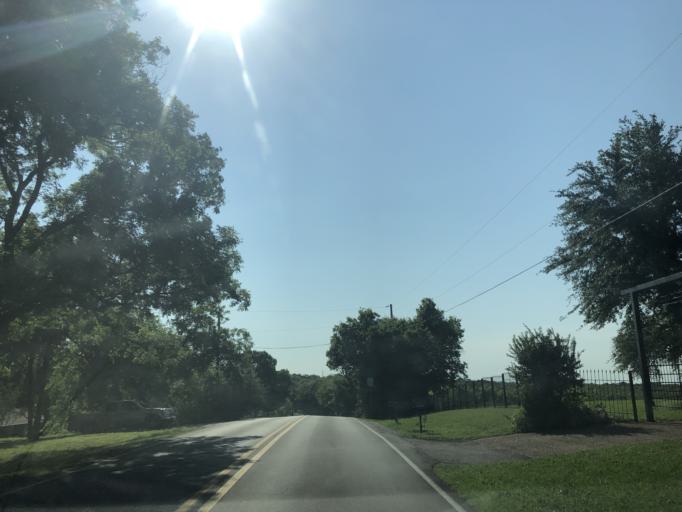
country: US
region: Texas
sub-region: Dallas County
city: Sunnyvale
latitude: 32.8288
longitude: -96.5727
